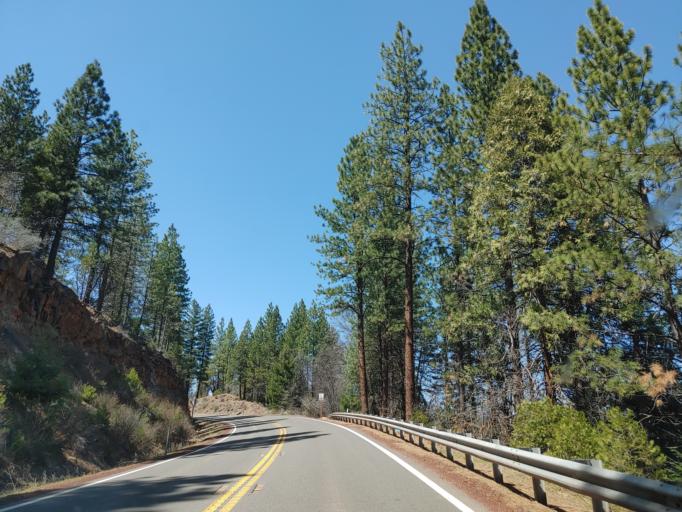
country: US
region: California
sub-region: Shasta County
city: Burney
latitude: 41.0158
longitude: -121.6295
